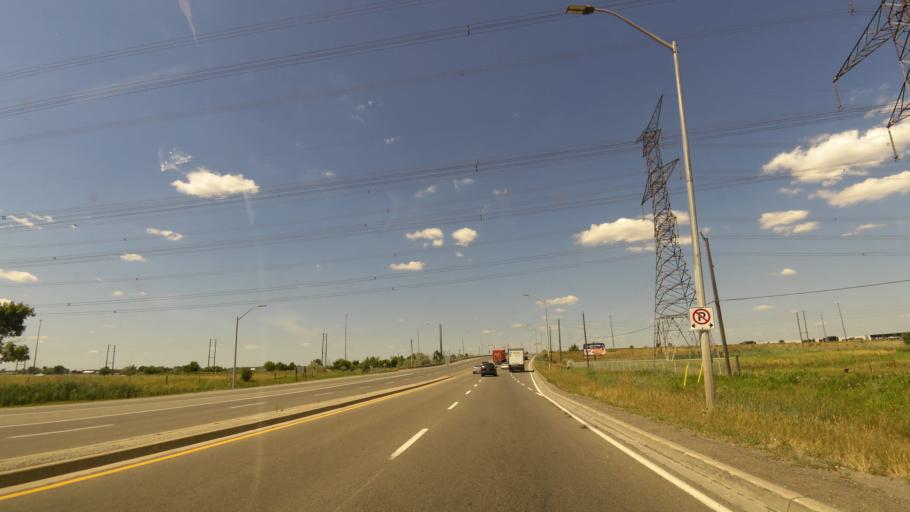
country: CA
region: Ontario
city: Brampton
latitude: 43.6018
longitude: -79.7899
